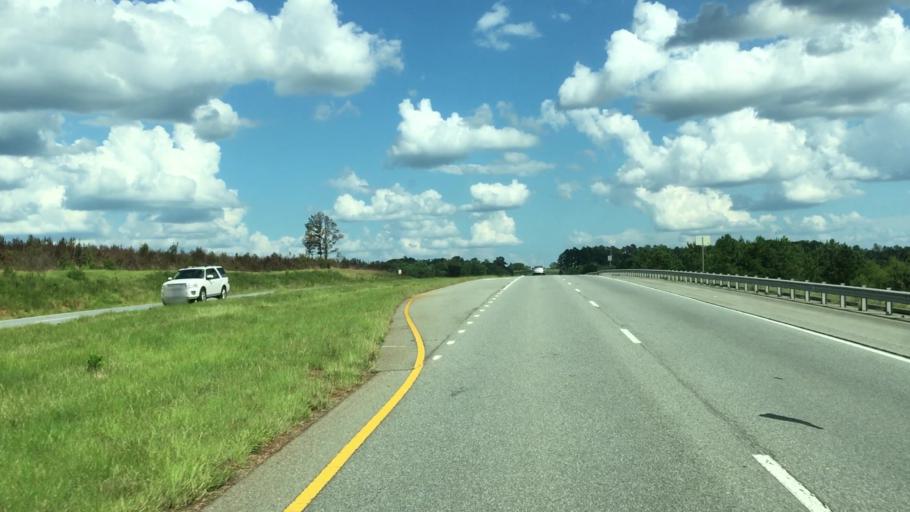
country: US
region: Georgia
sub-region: Wilkinson County
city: Irwinton
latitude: 32.6952
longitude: -83.1101
